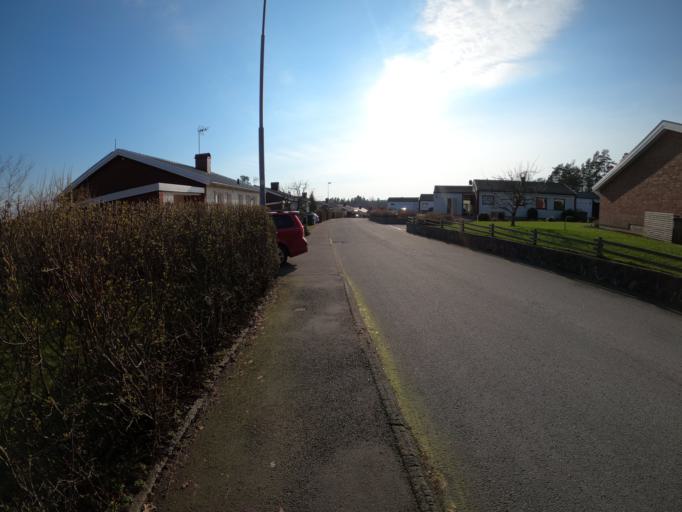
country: SE
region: Vaestra Goetaland
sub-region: Harryda Kommun
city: Molnlycke
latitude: 57.6514
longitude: 12.1159
